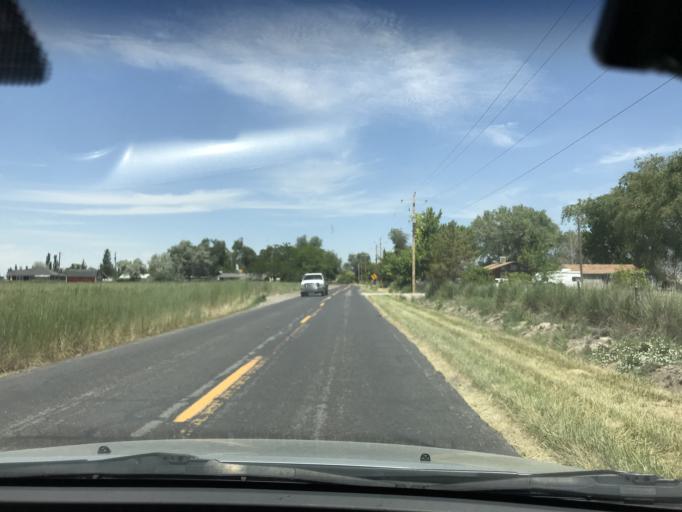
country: US
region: Utah
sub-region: Davis County
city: North Salt Lake
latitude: 40.8329
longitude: -111.9535
